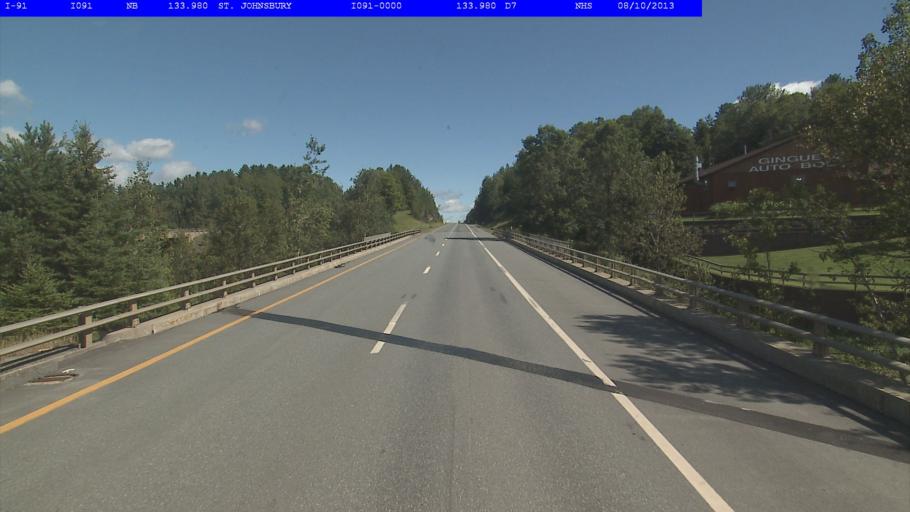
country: US
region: Vermont
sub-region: Caledonia County
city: Lyndon
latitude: 44.4742
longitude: -72.0244
